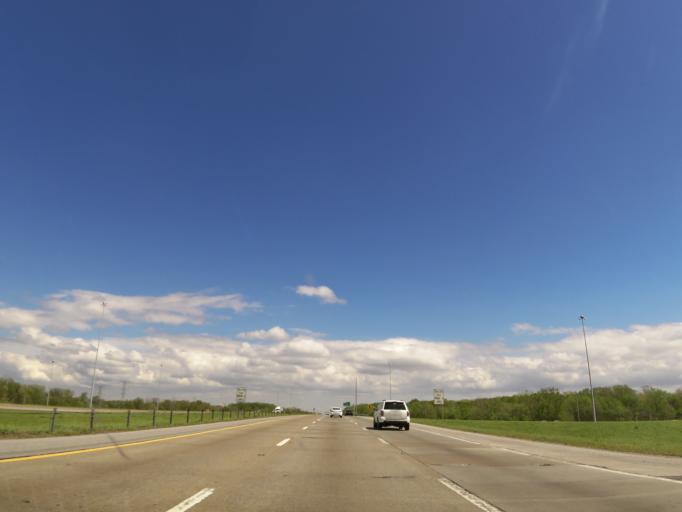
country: US
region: Tennessee
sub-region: Shelby County
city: Memphis
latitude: 35.1918
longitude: -89.9788
